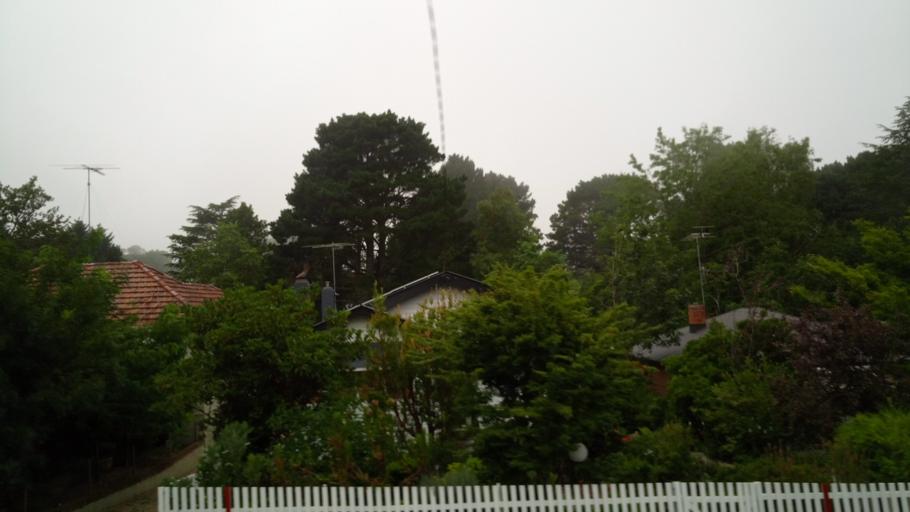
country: AU
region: New South Wales
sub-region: Blue Mountains Municipality
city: Leura
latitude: -33.7165
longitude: 150.3295
